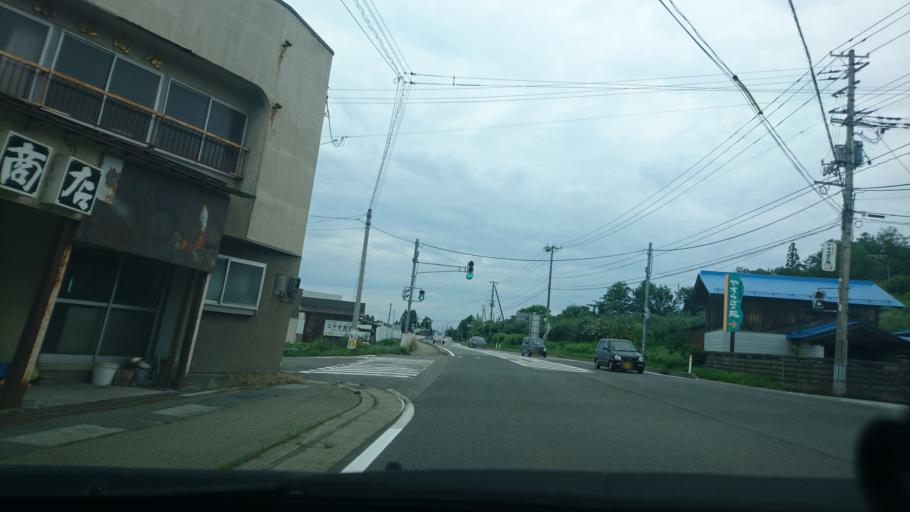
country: JP
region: Akita
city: Yokotemachi
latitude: 39.3533
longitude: 140.5626
